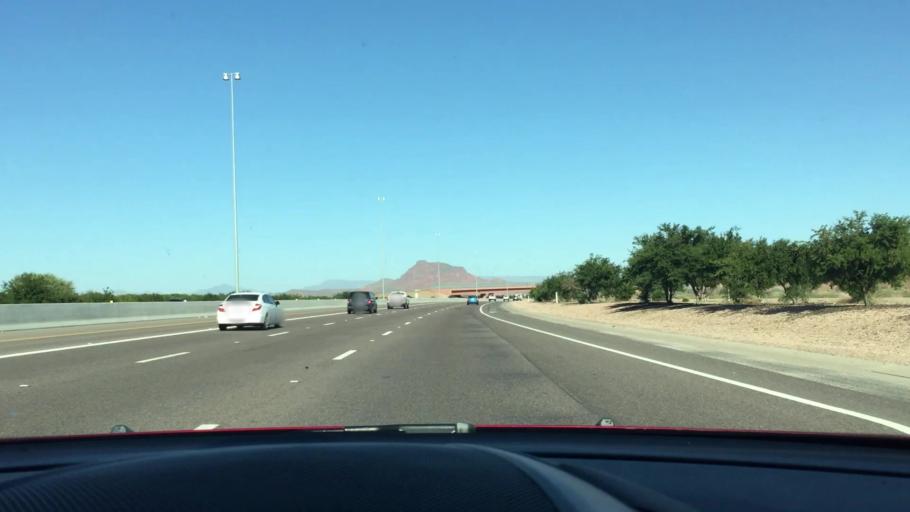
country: US
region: Arizona
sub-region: Maricopa County
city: Mesa
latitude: 33.4784
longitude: -111.7750
